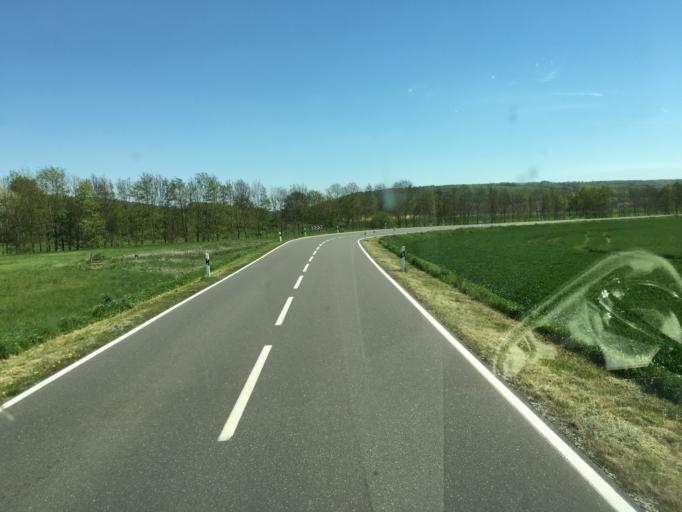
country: DE
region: Thuringia
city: Rossleben
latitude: 51.2725
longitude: 11.4787
